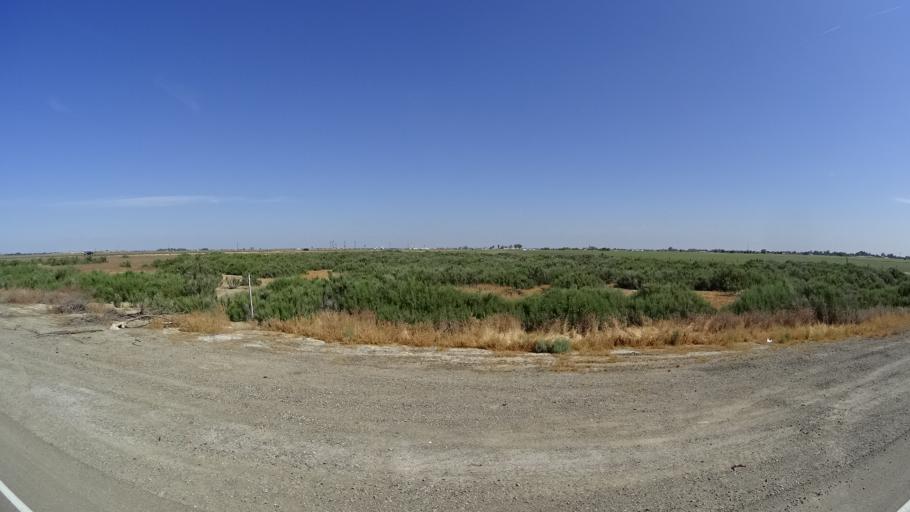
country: US
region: California
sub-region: Kings County
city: Lemoore
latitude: 36.2548
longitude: -119.8065
